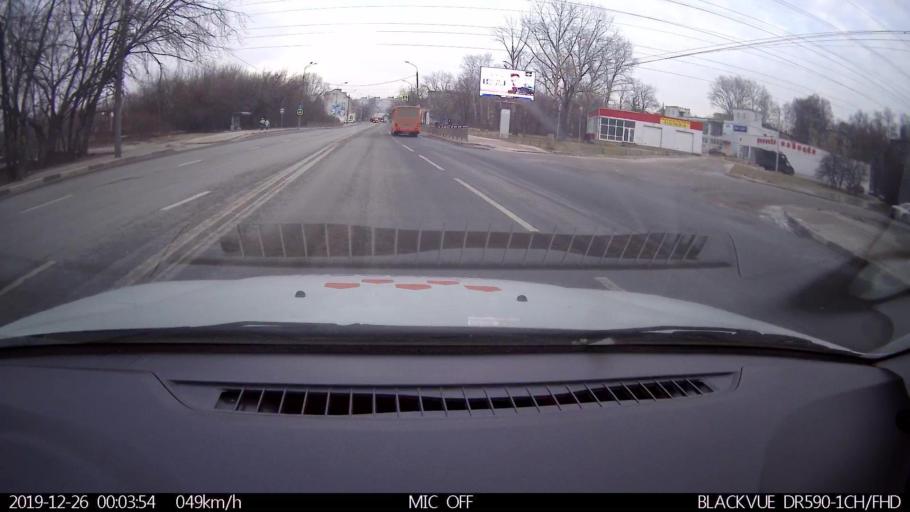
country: RU
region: Nizjnij Novgorod
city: Gorbatovka
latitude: 56.3452
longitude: 43.8419
